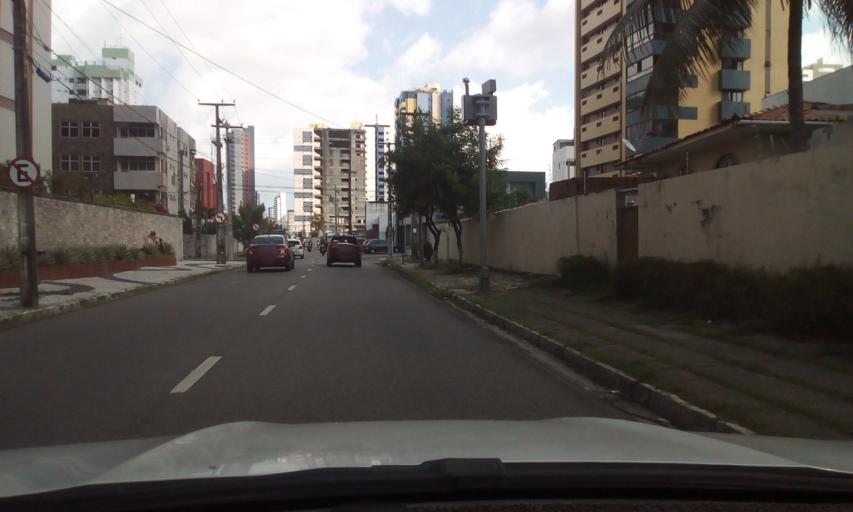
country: BR
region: Paraiba
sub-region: Joao Pessoa
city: Joao Pessoa
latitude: -7.0994
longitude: -34.8379
